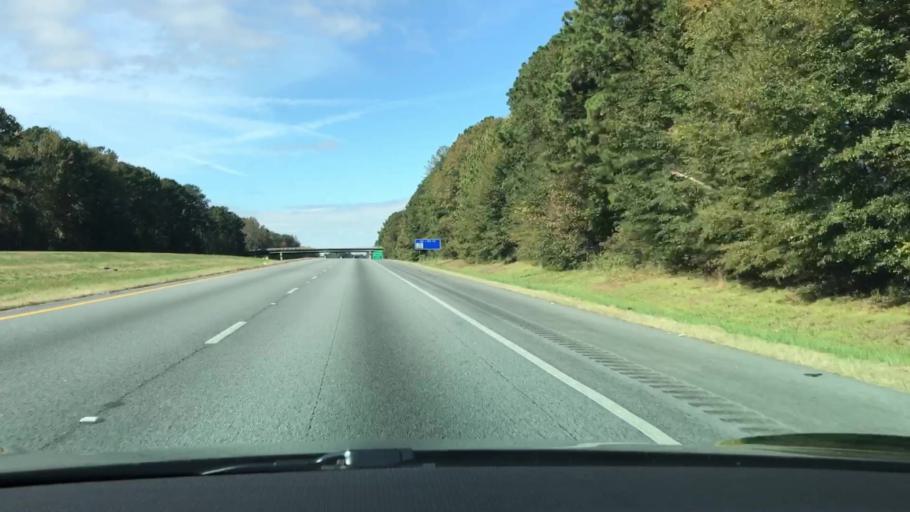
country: US
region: Georgia
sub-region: Walton County
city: Social Circle
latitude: 33.5859
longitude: -83.6061
